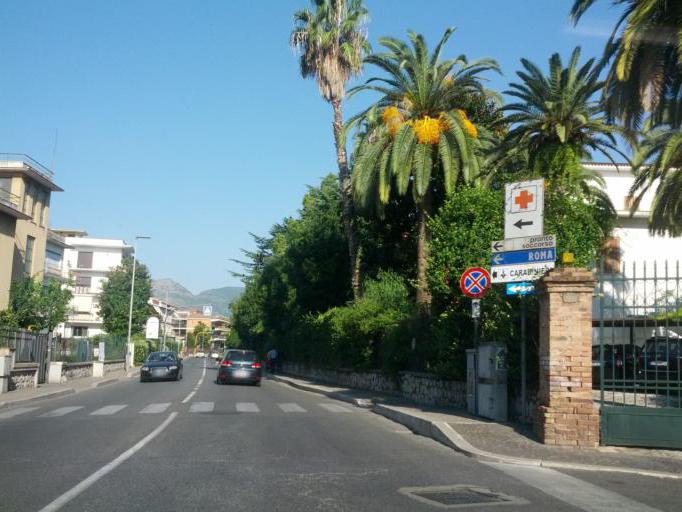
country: IT
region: Latium
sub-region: Provincia di Latina
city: Fondi
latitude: 41.3557
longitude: 13.4294
